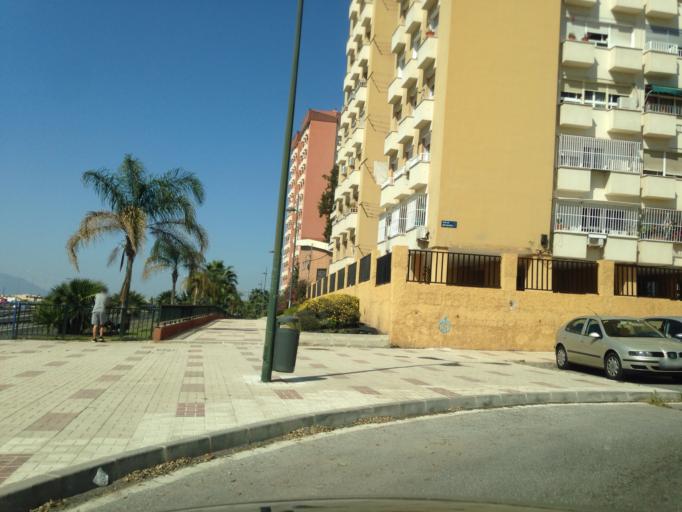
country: ES
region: Andalusia
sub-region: Provincia de Malaga
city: Malaga
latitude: 36.7149
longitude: -4.4509
